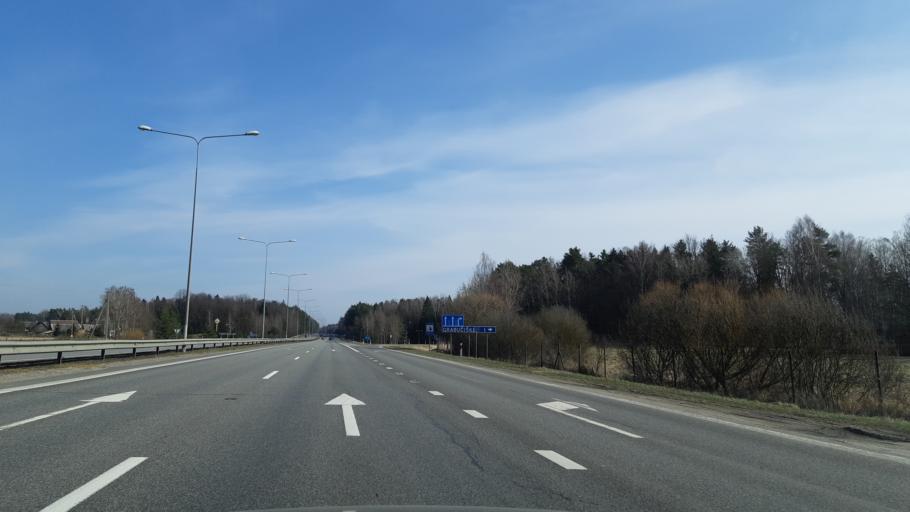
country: LT
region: Kauno apskritis
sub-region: Kauno rajonas
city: Karmelava
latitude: 54.8973
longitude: 24.1451
